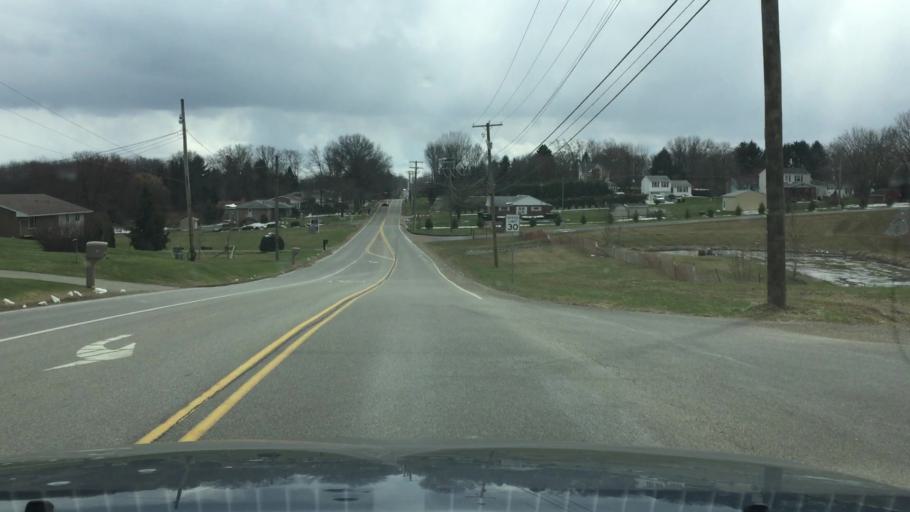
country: US
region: Pennsylvania
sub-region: Butler County
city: Homeacre-Lyndora
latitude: 40.8888
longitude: -79.9412
